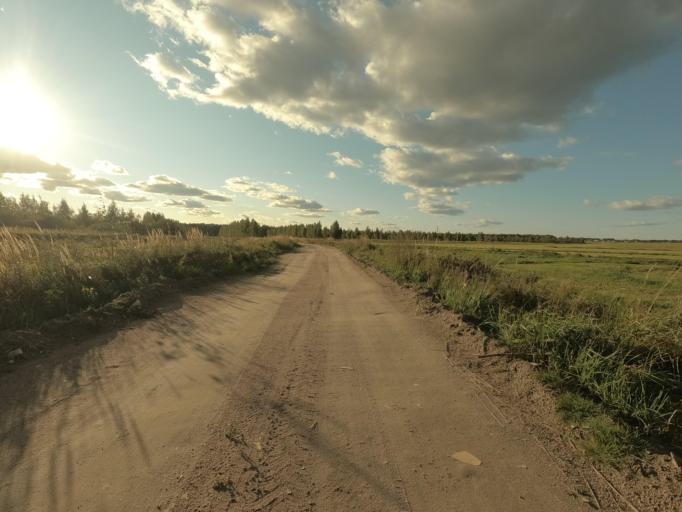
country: RU
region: Leningrad
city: Imeni Sverdlova
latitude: 59.8596
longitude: 30.7348
